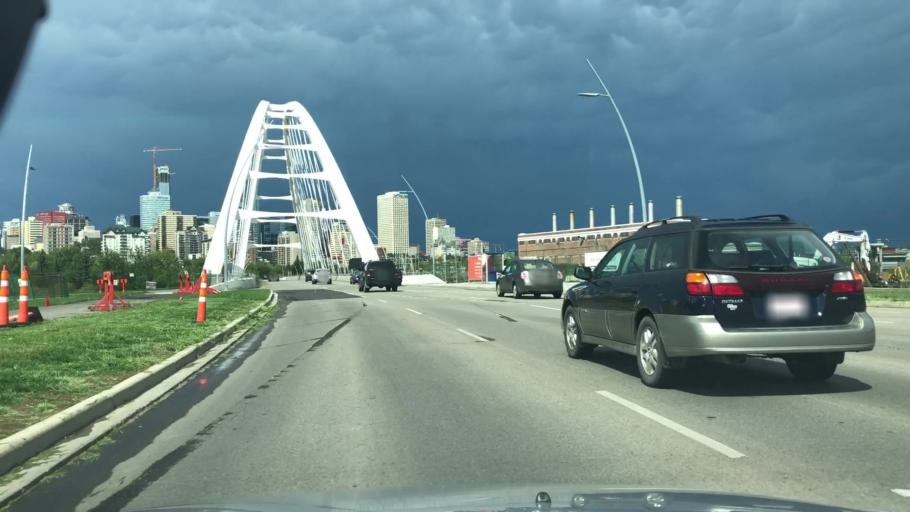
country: CA
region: Alberta
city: Edmonton
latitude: 53.5265
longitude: -113.5029
